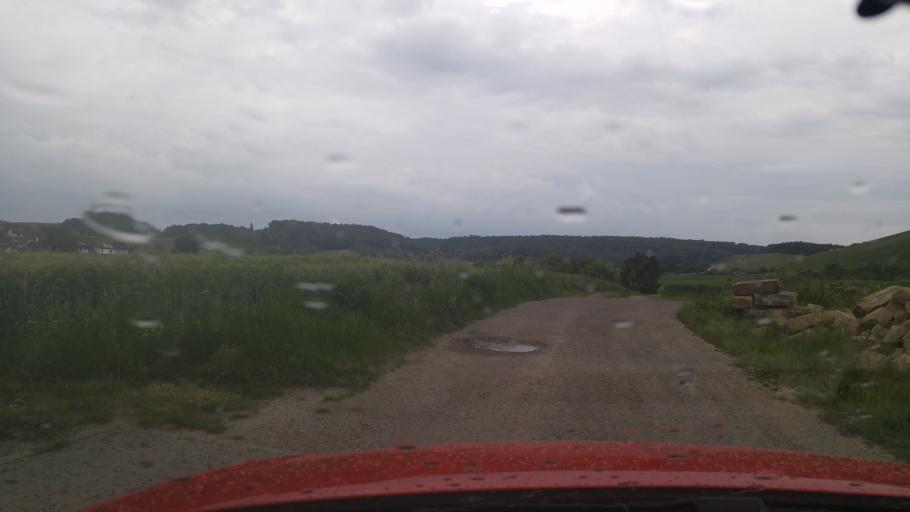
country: DE
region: Baden-Wuerttemberg
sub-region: Regierungsbezirk Stuttgart
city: Pfaffenhofen
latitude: 49.1032
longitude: 8.9719
